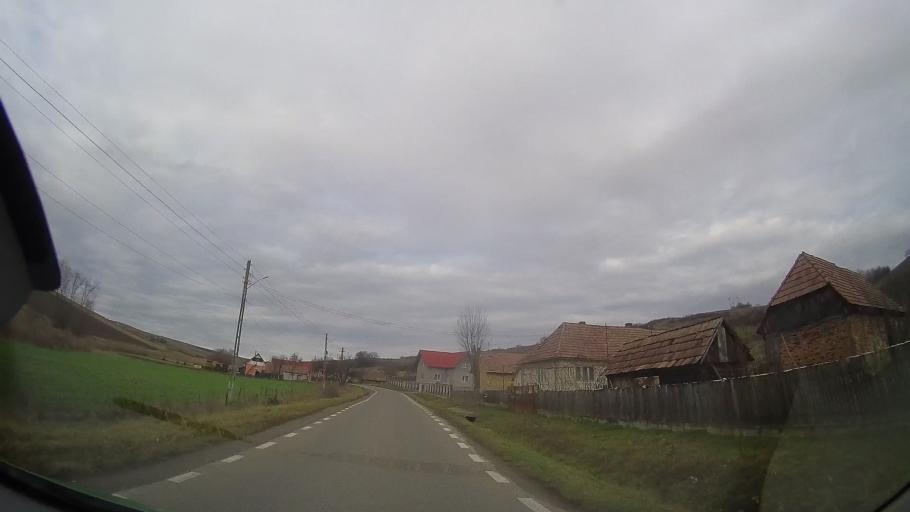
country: RO
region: Mures
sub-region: Comuna Cozma
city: Cozma
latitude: 46.8131
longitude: 24.4986
